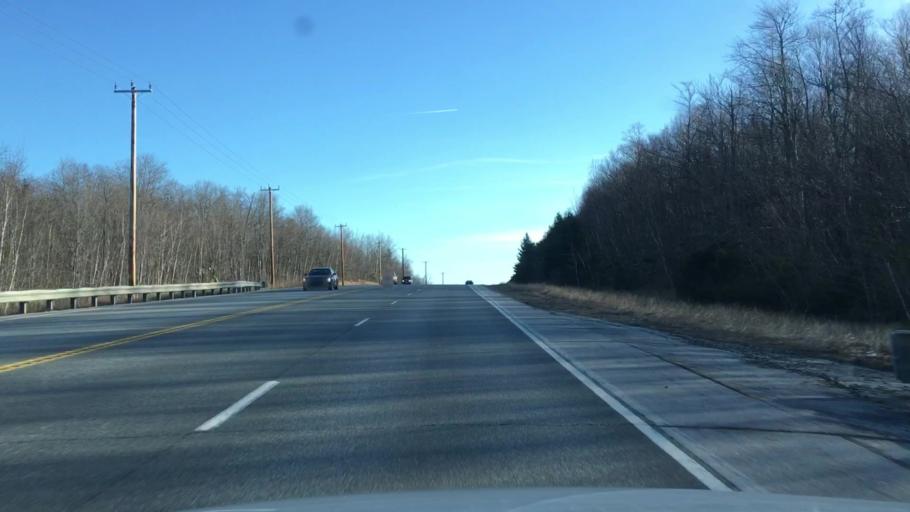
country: US
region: Maine
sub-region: Hancock County
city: Dedham
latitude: 44.6922
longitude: -68.5886
